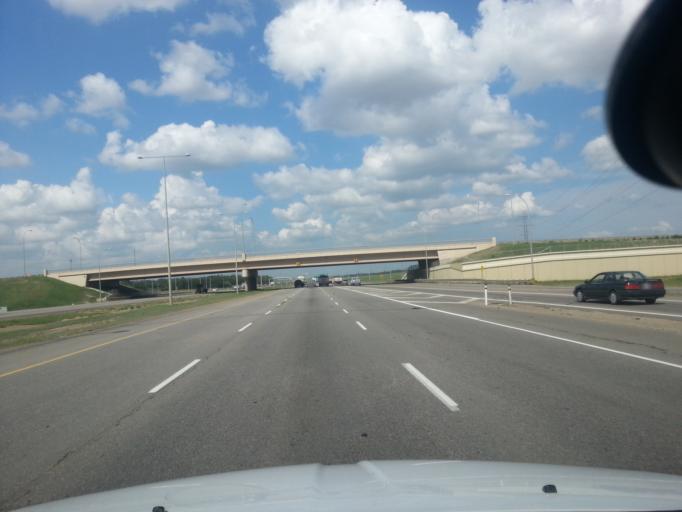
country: CA
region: Alberta
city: St. Albert
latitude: 53.5213
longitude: -113.6590
